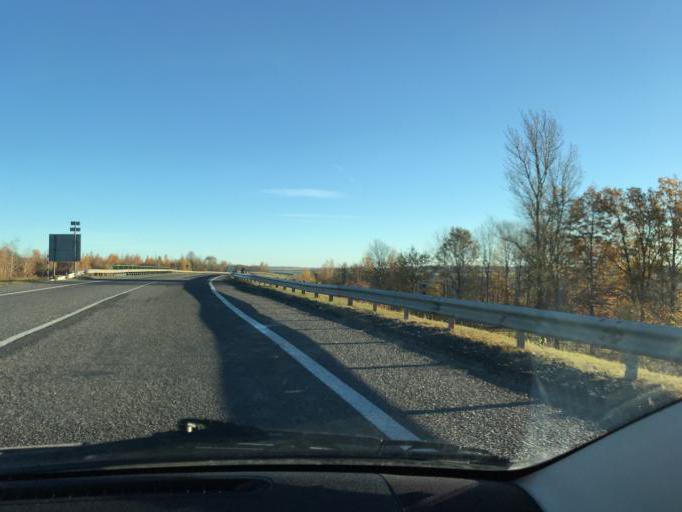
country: BY
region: Vitebsk
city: Vitebsk
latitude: 55.1057
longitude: 30.3034
